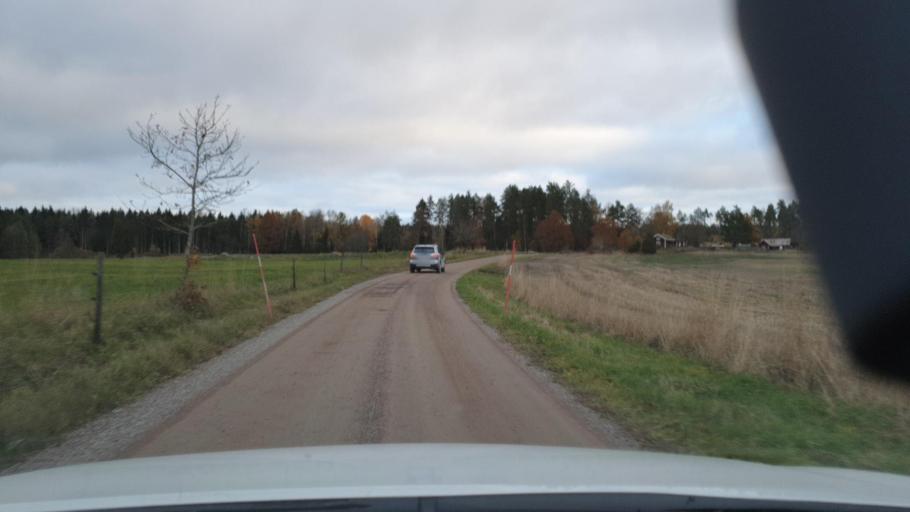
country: SE
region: Kalmar
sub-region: Hultsfreds Kommun
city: Malilla
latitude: 57.3296
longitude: 15.8111
